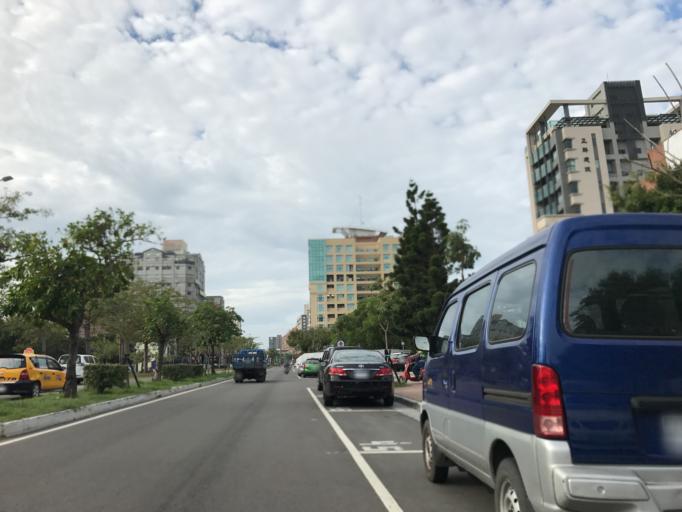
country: TW
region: Taiwan
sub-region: Hsinchu
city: Hsinchu
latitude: 24.8121
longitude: 120.9692
